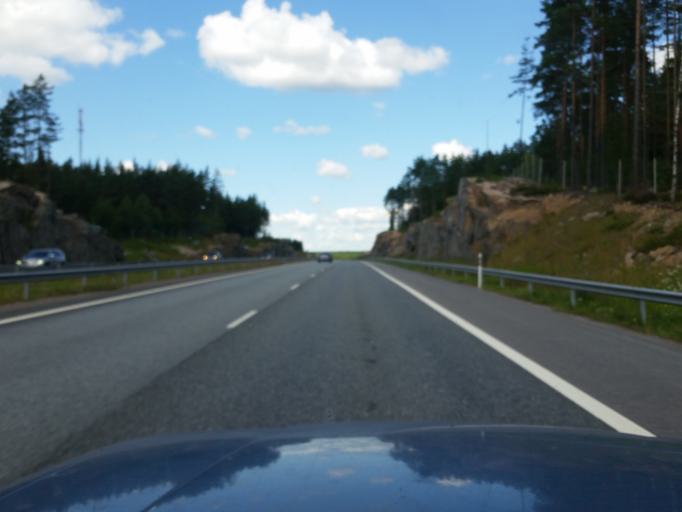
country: FI
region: Varsinais-Suomi
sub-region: Salo
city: Suomusjaervi
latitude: 60.3732
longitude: 23.6461
